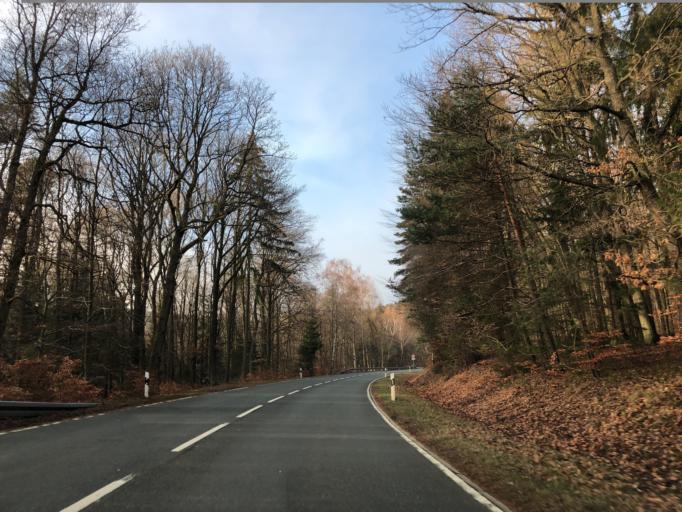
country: DE
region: Hesse
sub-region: Regierungsbezirk Darmstadt
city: Kronberg
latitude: 50.2307
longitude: 8.5038
